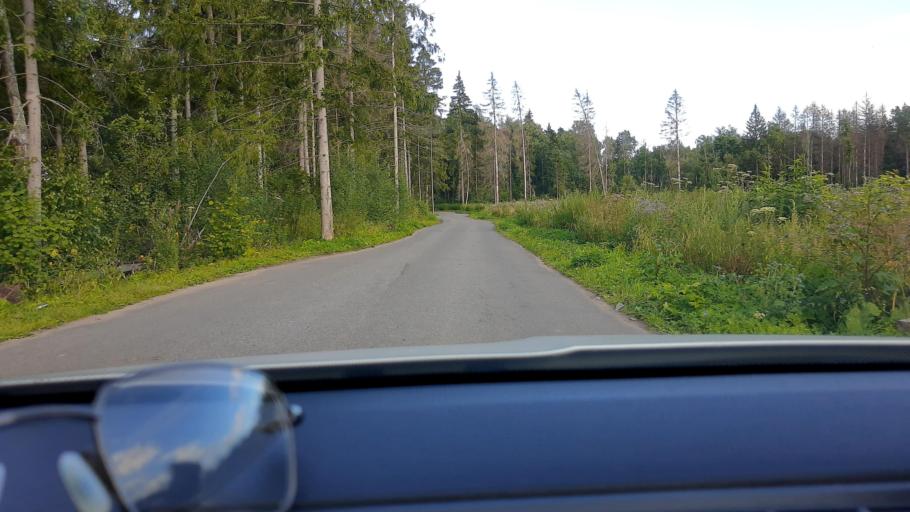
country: RU
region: Moskovskaya
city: Nazar'yevo
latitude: 55.6910
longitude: 37.0454
